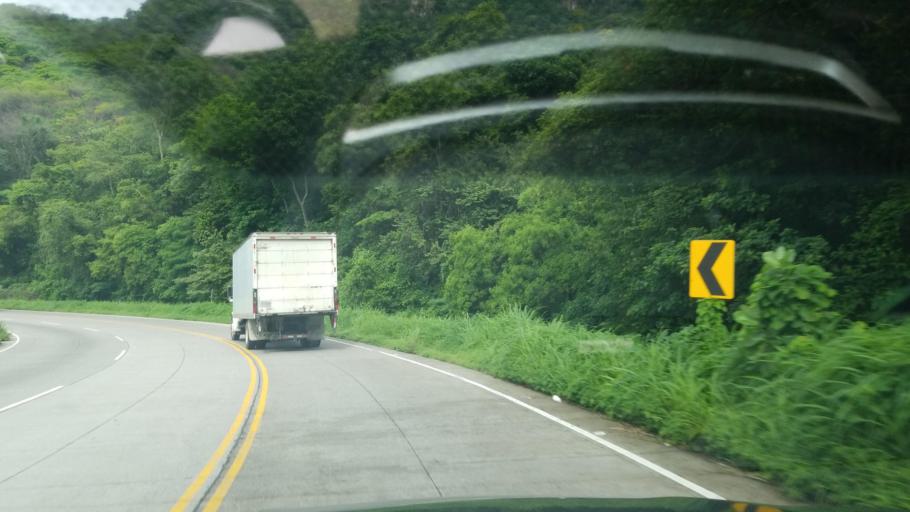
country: HN
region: Francisco Morazan
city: El Porvenir
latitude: 13.7182
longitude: -87.3180
